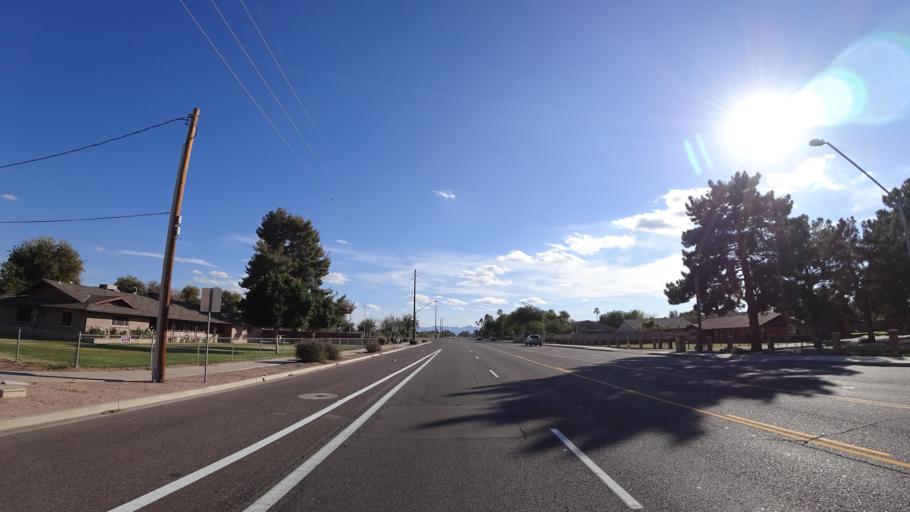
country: US
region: Arizona
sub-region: Maricopa County
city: Glendale
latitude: 33.5268
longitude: -112.2376
